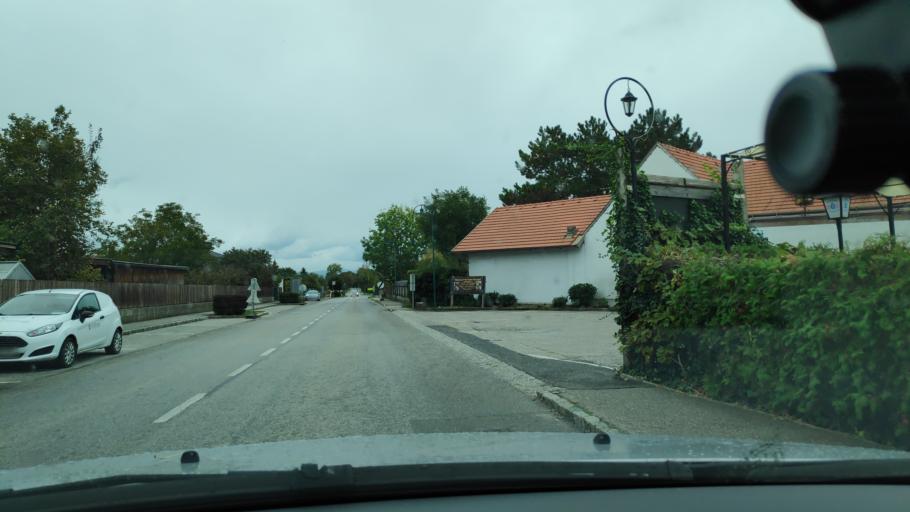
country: AT
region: Lower Austria
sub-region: Politischer Bezirk Neunkirchen
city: Willendorf am Steinfelde
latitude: 47.7883
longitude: 16.0574
